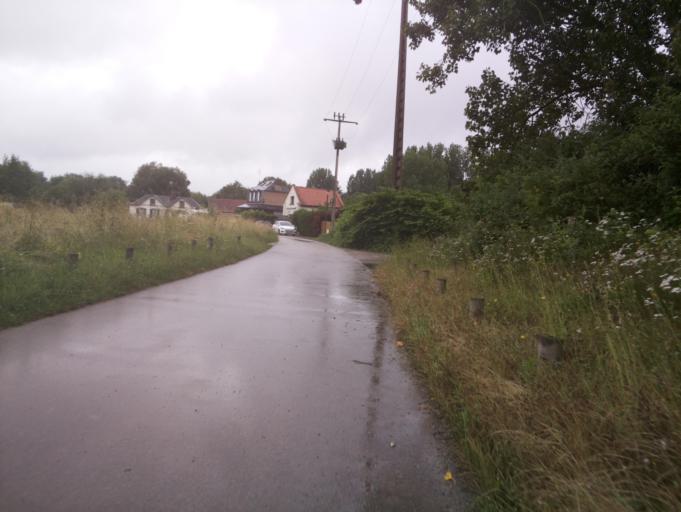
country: FR
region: Picardie
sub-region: Departement de la Somme
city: Dreuil-les-Amiens
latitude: 49.9179
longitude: 2.2326
